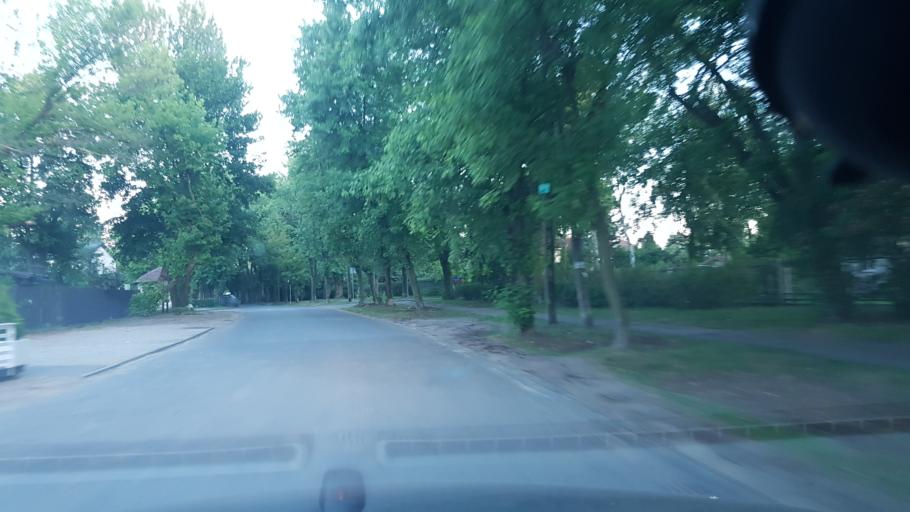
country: PL
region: Masovian Voivodeship
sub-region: Powiat otwocki
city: Jozefow
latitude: 52.1662
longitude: 21.2130
